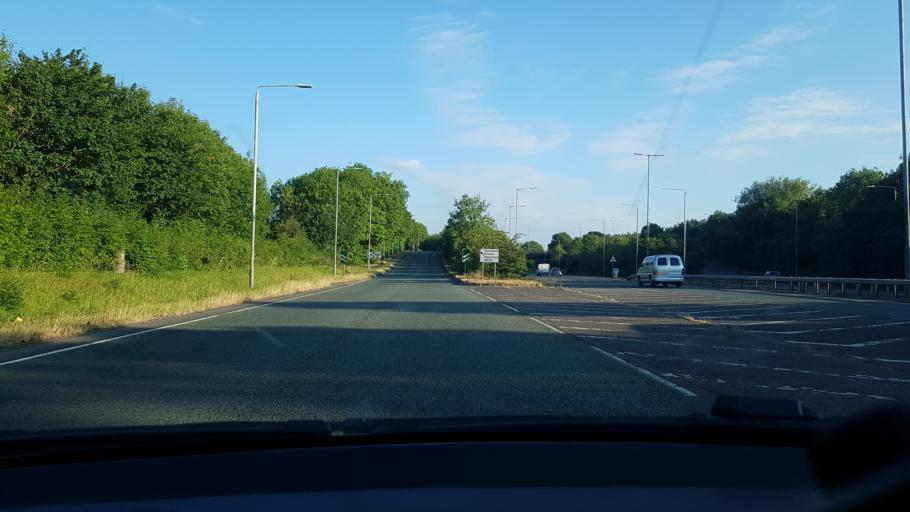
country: GB
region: England
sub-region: Nottinghamshire
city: Eastwood
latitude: 53.0156
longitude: -1.3183
